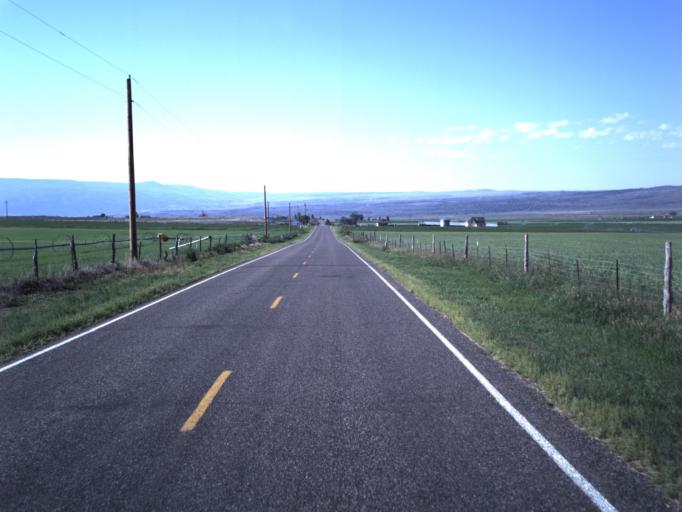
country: US
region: Utah
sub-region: Wayne County
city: Loa
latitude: 38.4306
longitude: -111.6203
